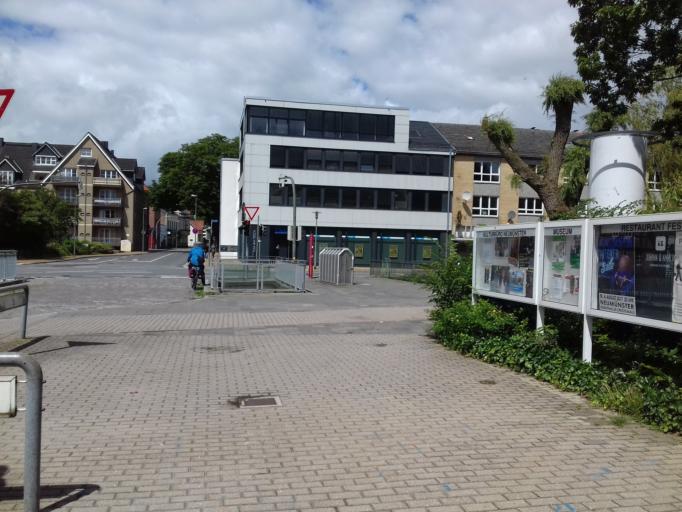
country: DE
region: Schleswig-Holstein
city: Neumunster
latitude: 54.0721
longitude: 9.9816
